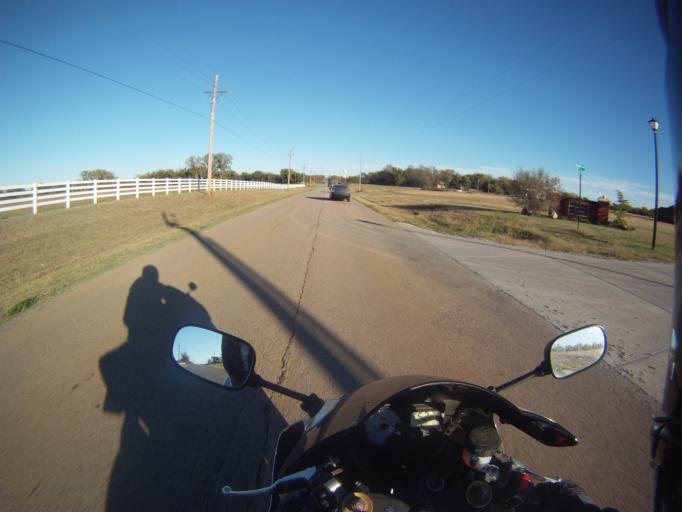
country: US
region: Oklahoma
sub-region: Payne County
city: Stillwater
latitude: 36.1303
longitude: -97.1123
